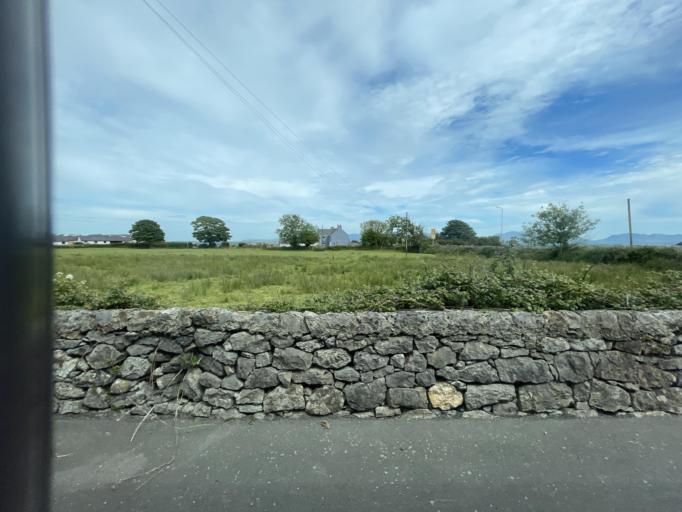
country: GB
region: Wales
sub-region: Anglesey
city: Llangefni
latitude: 53.2436
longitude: -4.3443
